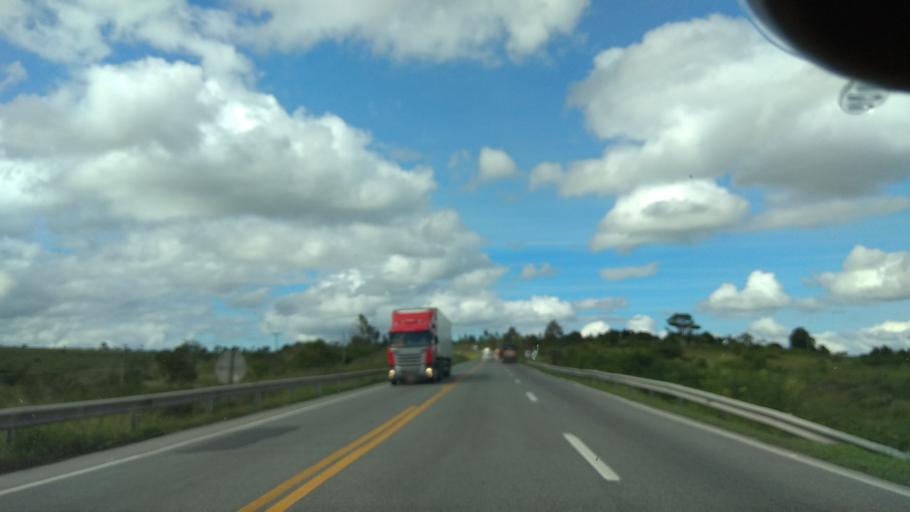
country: BR
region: Bahia
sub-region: Santa Ines
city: Santa Ines
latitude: -13.1081
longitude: -39.9741
